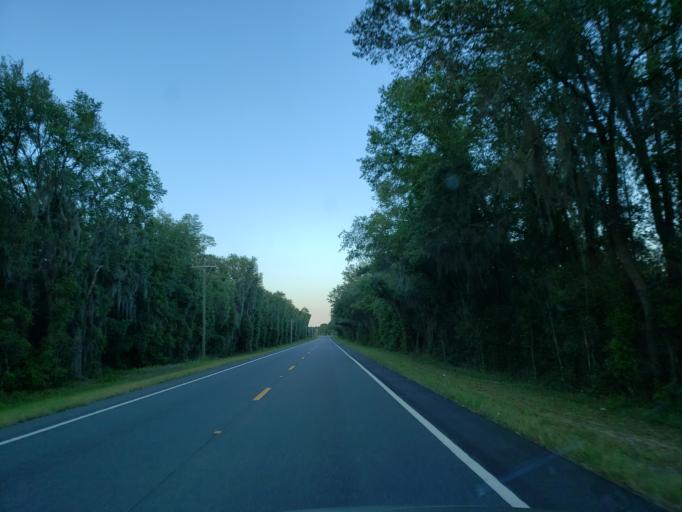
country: US
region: Georgia
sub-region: Echols County
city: Statenville
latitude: 30.5813
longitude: -83.1788
